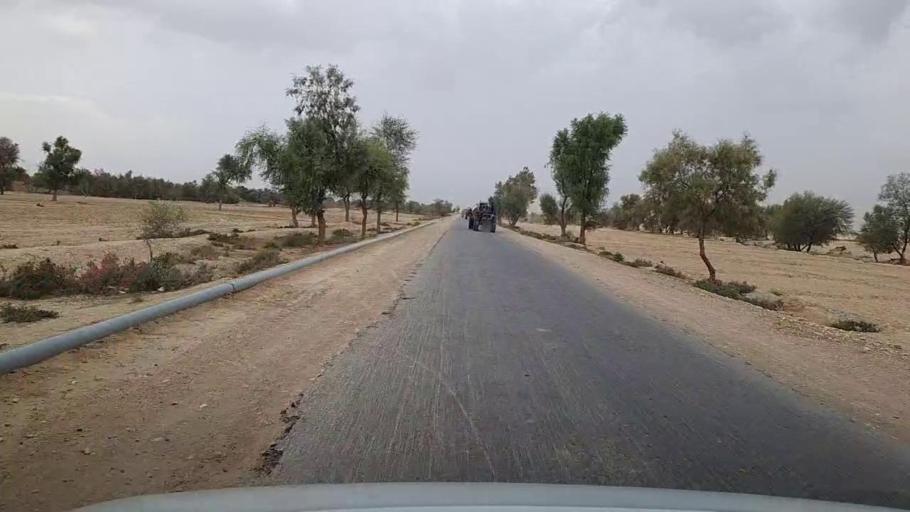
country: PK
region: Sindh
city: Sehwan
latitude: 26.3271
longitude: 67.7255
